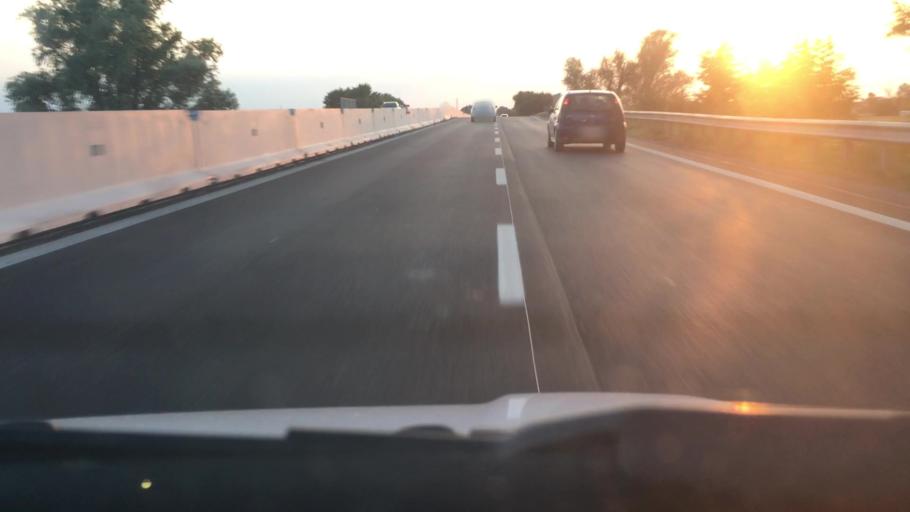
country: IT
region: Emilia-Romagna
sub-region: Provincia di Ferrara
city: Cona
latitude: 44.7969
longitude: 11.6815
